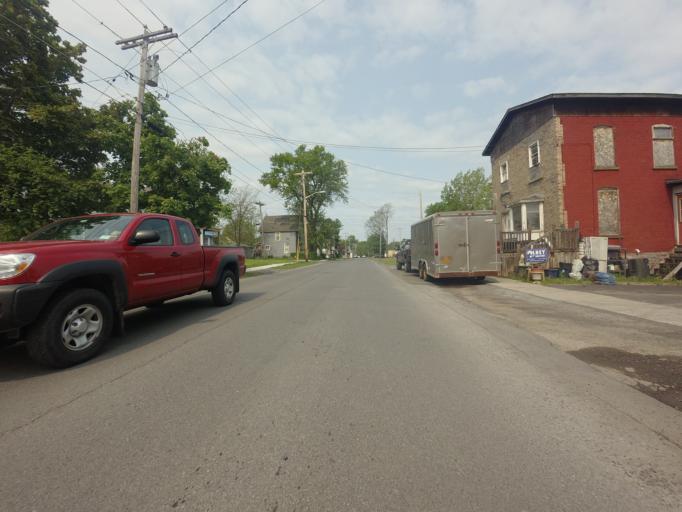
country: US
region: New York
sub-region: Jefferson County
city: Watertown
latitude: 43.9765
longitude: -75.8926
